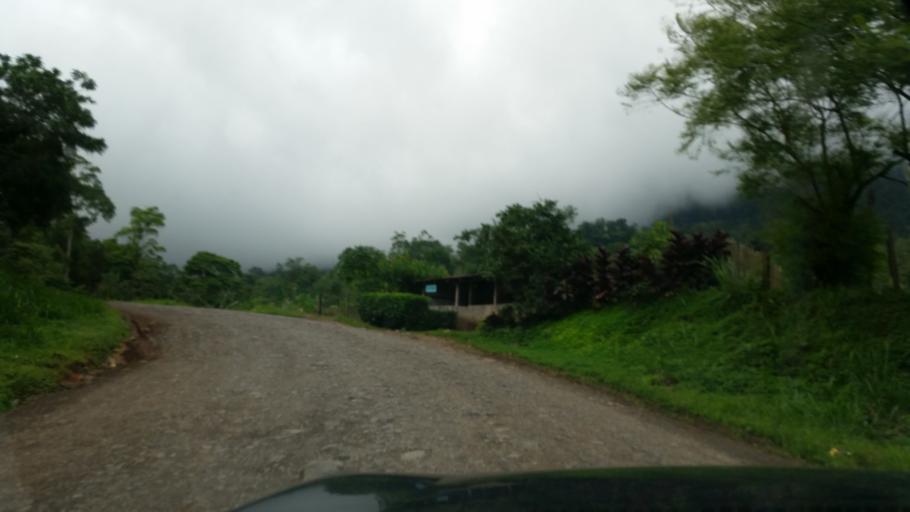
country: NI
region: Jinotega
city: San Jose de Bocay
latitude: 13.2764
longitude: -85.7259
